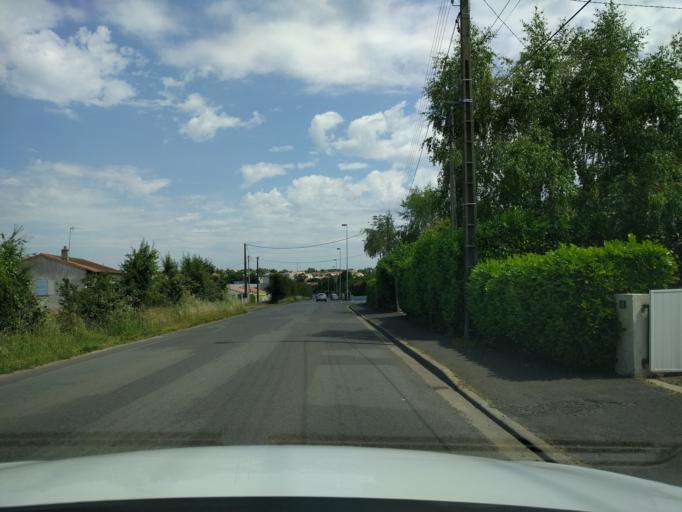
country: FR
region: Poitou-Charentes
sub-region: Departement des Deux-Sevres
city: Niort
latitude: 46.3435
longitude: -0.4860
